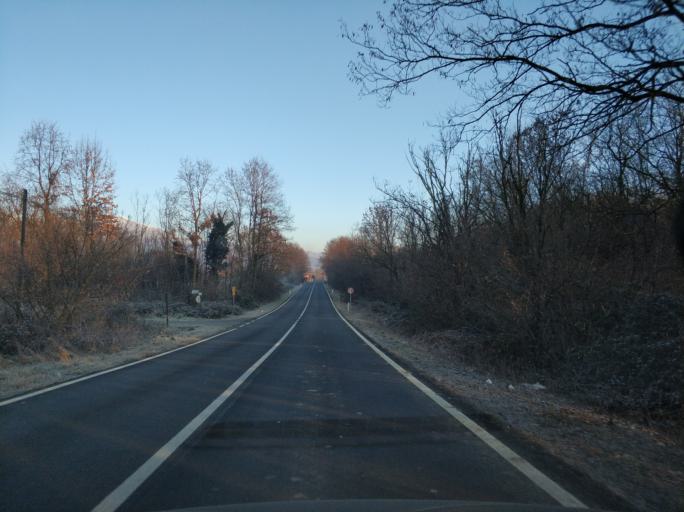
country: IT
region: Piedmont
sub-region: Provincia di Torino
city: Grosso
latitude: 45.2767
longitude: 7.5817
